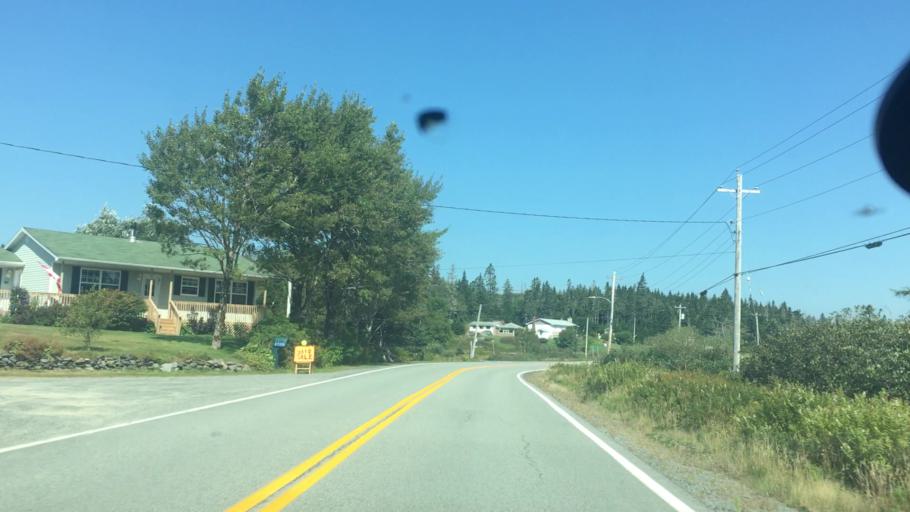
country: CA
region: Nova Scotia
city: New Glasgow
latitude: 44.9262
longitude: -62.2983
